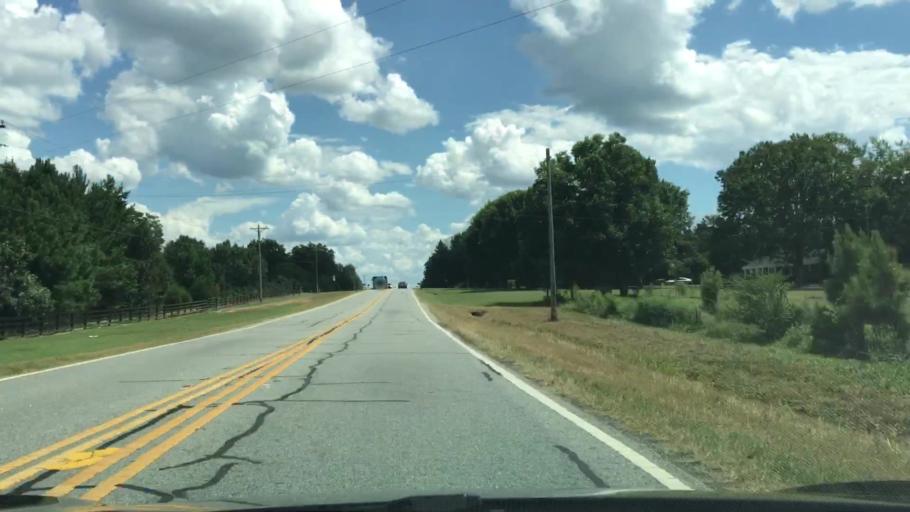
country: US
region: Georgia
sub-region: Oconee County
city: Watkinsville
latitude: 33.8330
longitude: -83.3794
